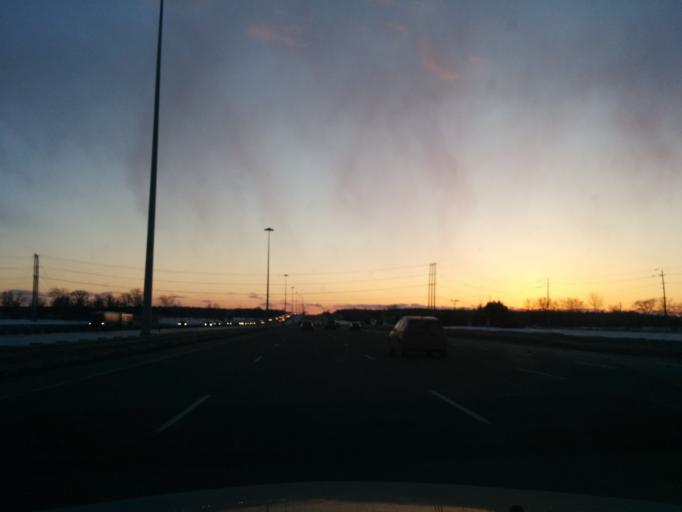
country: CA
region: Ontario
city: Bells Corners
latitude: 45.3380
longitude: -75.8431
